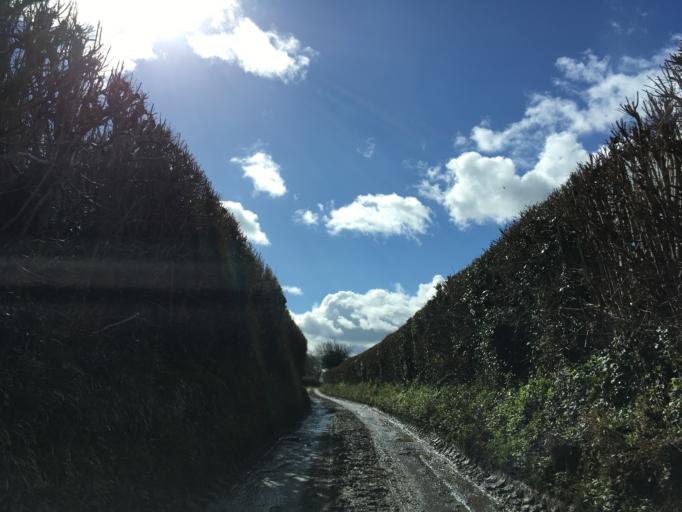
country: GB
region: England
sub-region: South Gloucestershire
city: Horton
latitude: 51.5799
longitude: -2.3383
